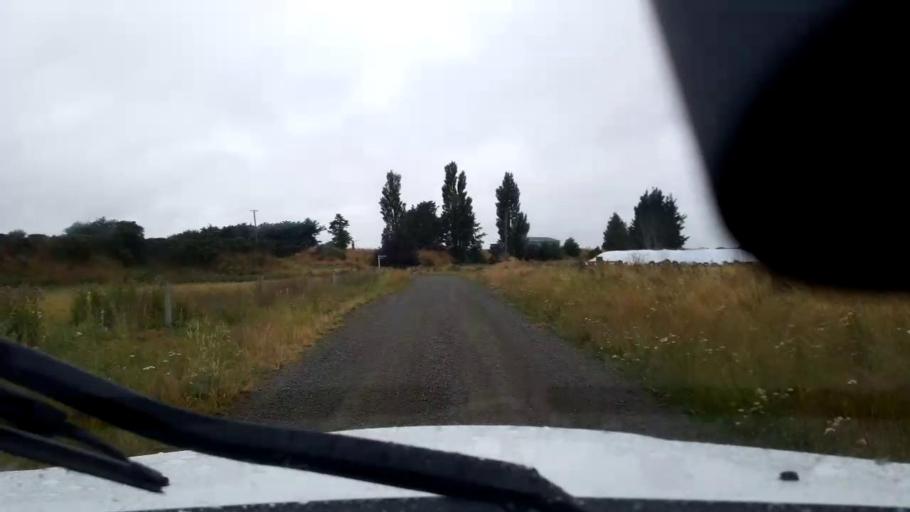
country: NZ
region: Canterbury
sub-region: Timaru District
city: Pleasant Point
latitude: -44.2533
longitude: 171.2171
